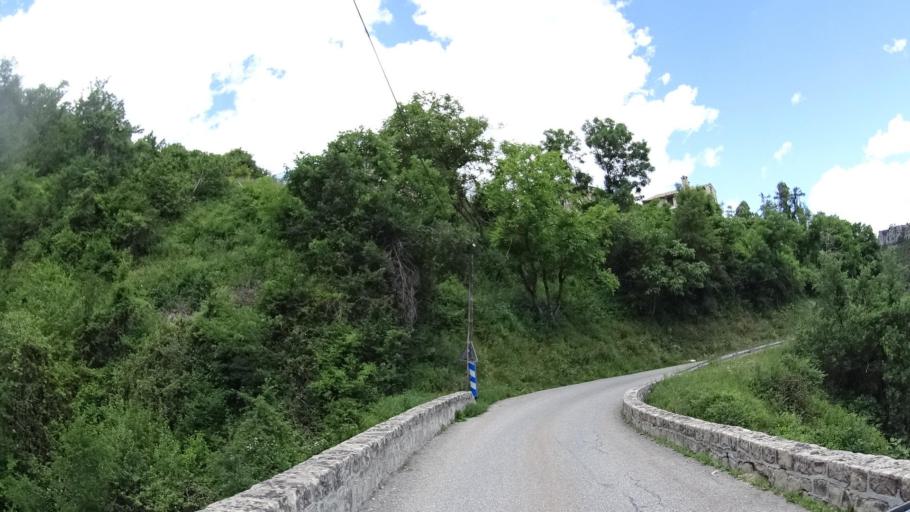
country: FR
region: Provence-Alpes-Cote d'Azur
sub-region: Departement des Alpes-de-Haute-Provence
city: Annot
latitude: 44.0184
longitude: 6.6277
